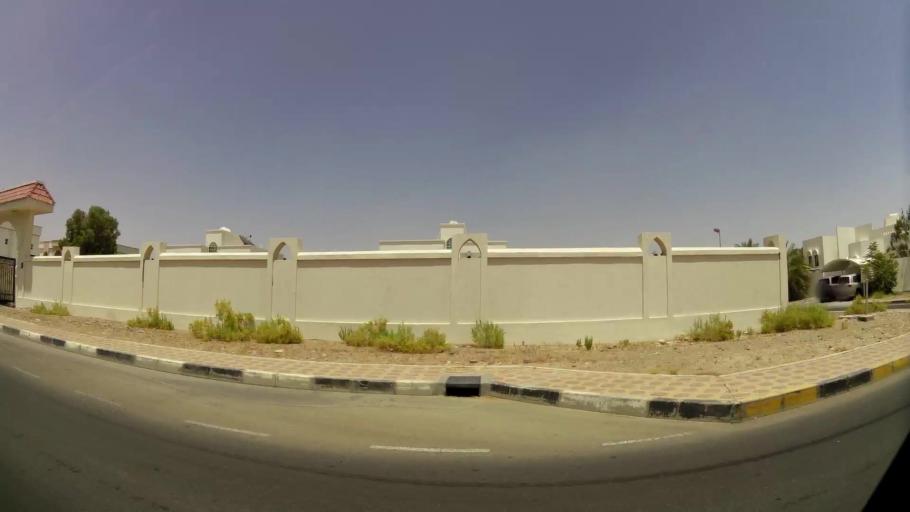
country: AE
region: Abu Dhabi
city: Al Ain
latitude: 24.2550
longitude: 55.7106
